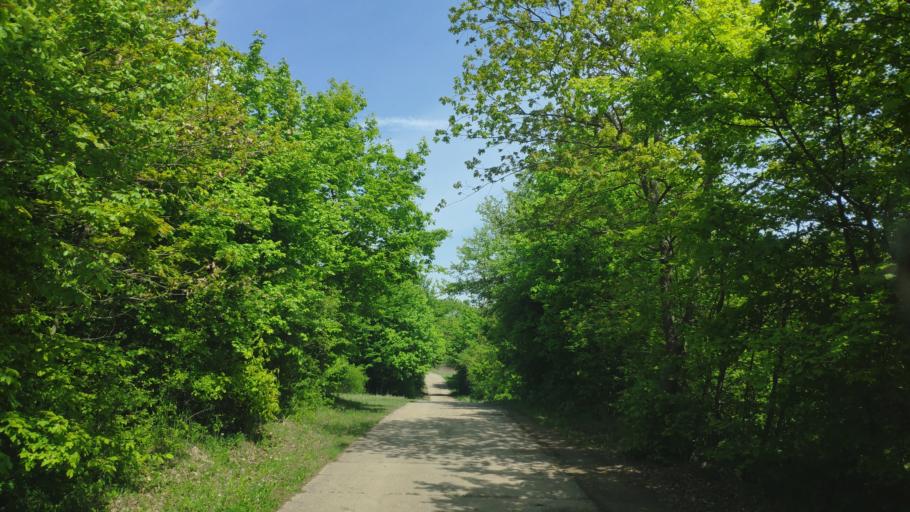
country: SK
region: Kosicky
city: Secovce
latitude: 48.6946
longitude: 21.5970
